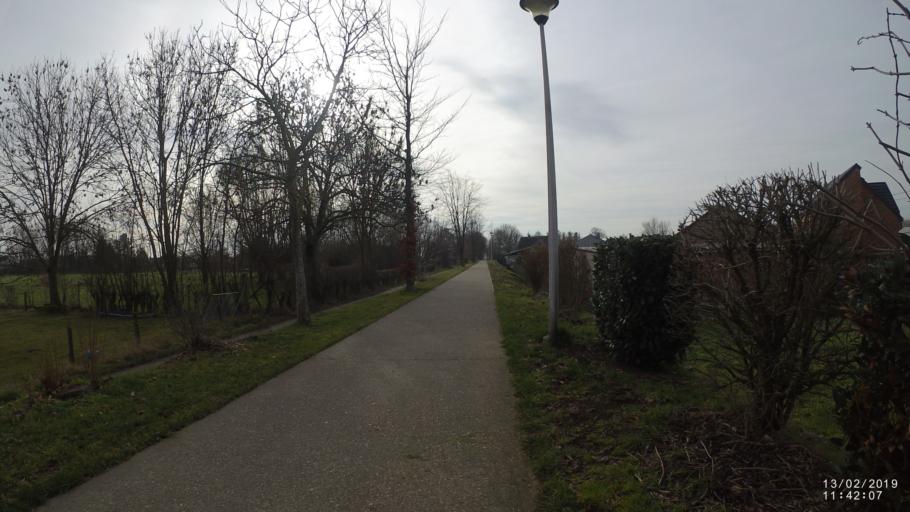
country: BE
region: Flanders
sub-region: Provincie Limburg
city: Halen
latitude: 50.9326
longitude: 5.1134
